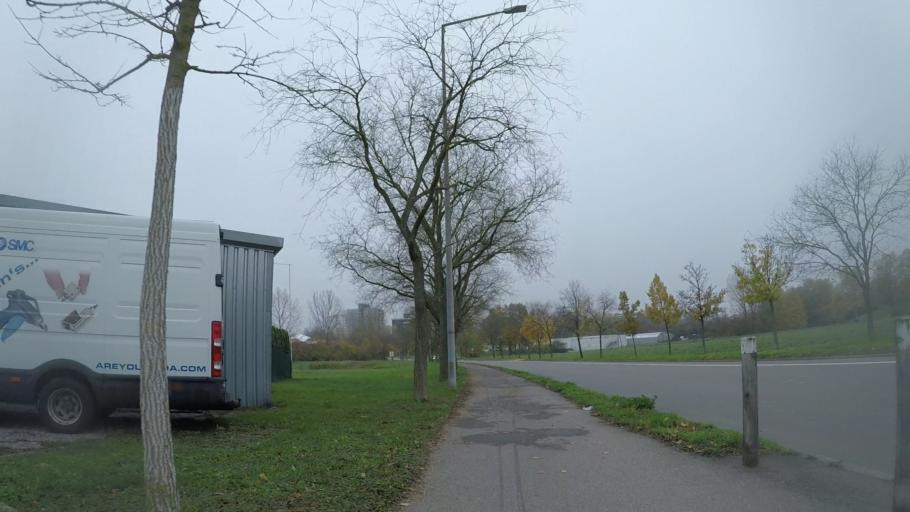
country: DE
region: Baden-Wuerttemberg
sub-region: Tuebingen Region
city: Reutlingen
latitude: 48.5155
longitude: 9.2166
